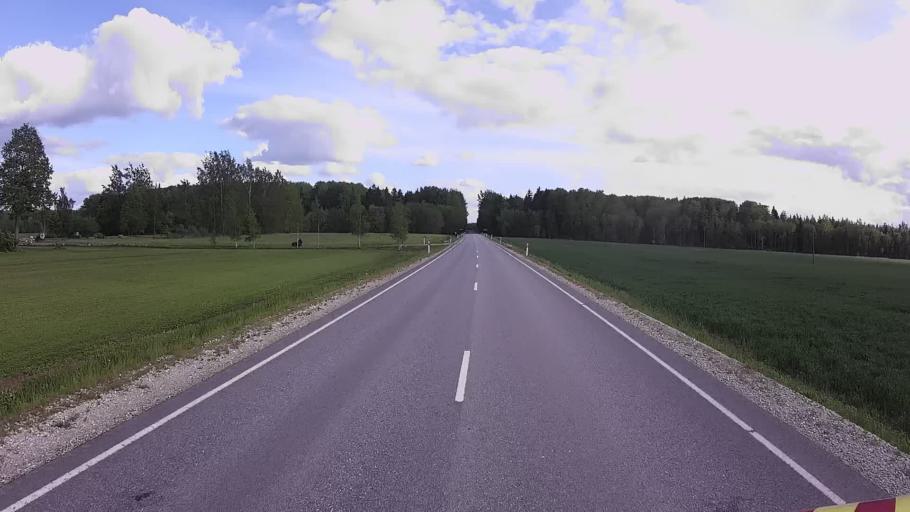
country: EE
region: Jogevamaa
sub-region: Mustvee linn
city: Mustvee
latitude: 58.8881
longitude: 26.8124
